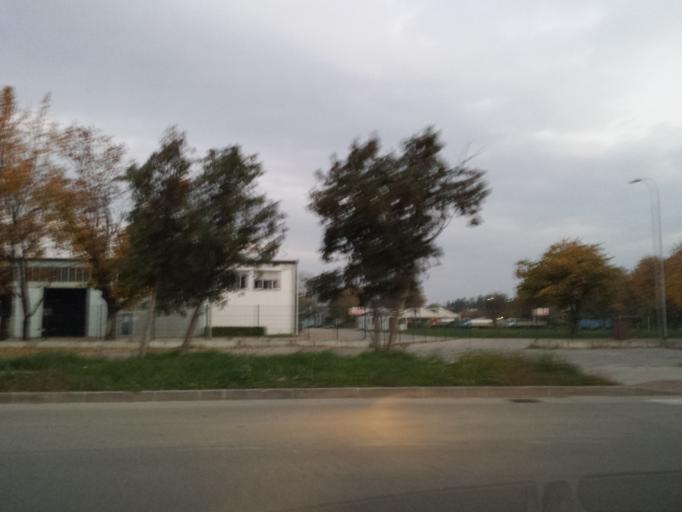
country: HR
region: Grad Zagreb
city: Novi Zagreb
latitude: 45.7992
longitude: 16.0079
